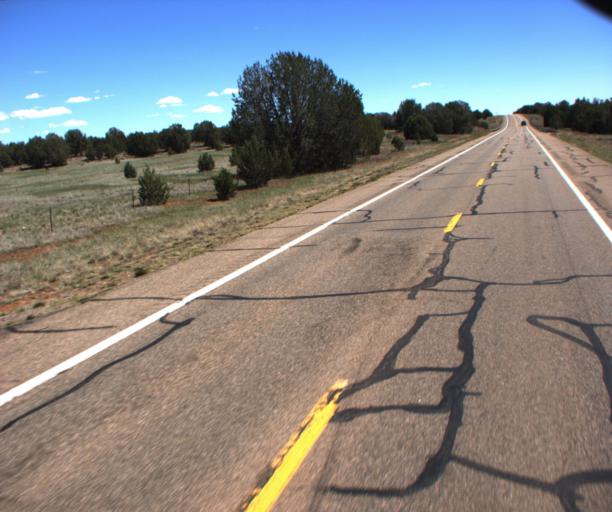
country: US
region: Arizona
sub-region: Yavapai County
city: Paulden
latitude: 35.1233
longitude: -112.4354
